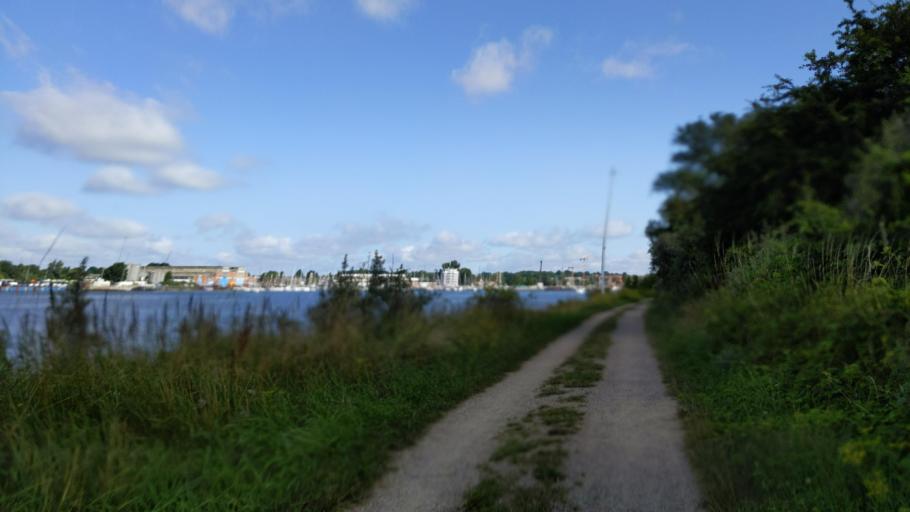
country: DE
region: Schleswig-Holstein
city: Travemuende
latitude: 53.9471
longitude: 10.8631
